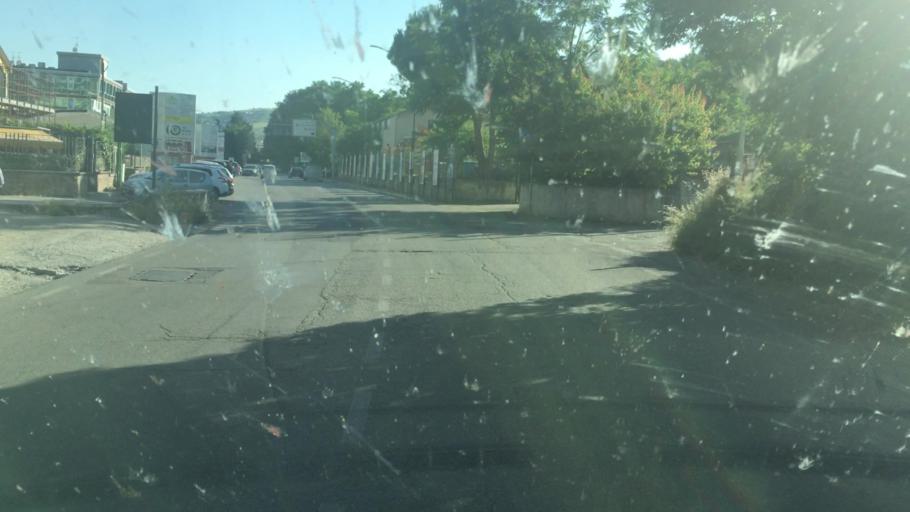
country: IT
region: Basilicate
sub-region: Provincia di Potenza
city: Potenza
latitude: 40.6338
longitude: 15.8138
